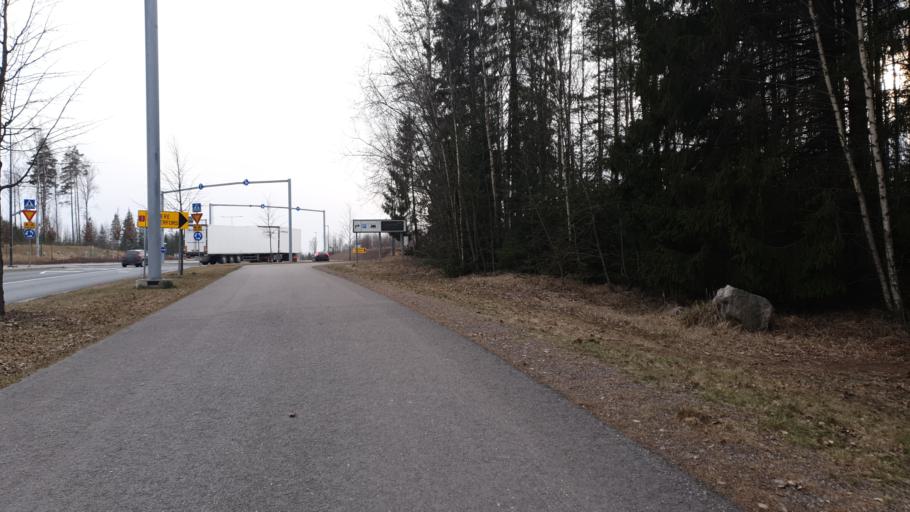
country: FI
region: Uusimaa
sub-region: Helsinki
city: Kilo
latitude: 60.3135
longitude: 24.8555
